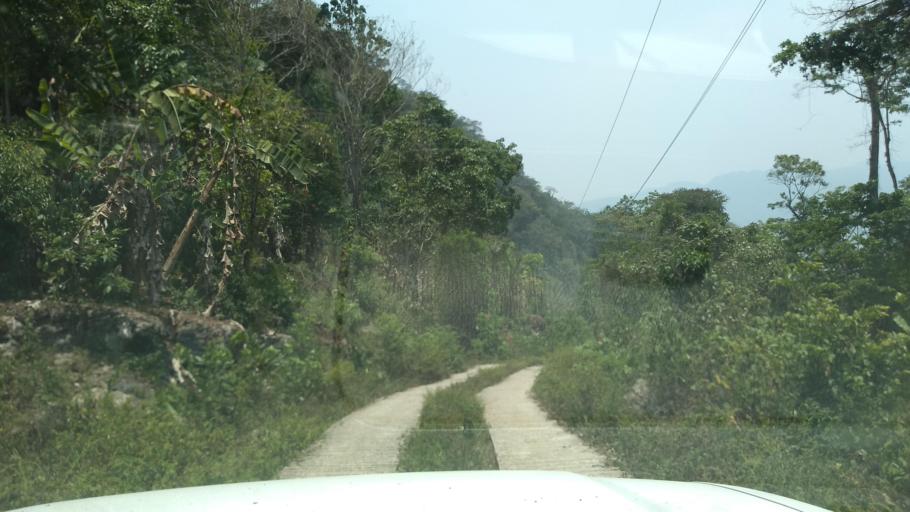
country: MX
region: Veracruz
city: Motzorongo
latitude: 18.5984
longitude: -96.7373
